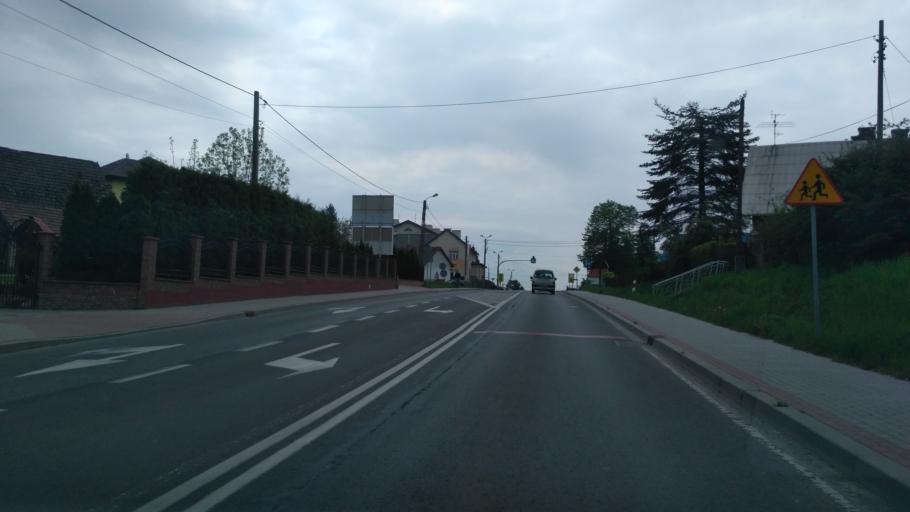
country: PL
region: Lesser Poland Voivodeship
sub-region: Powiat tarnowski
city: Tarnowiec
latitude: 49.9835
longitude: 20.9853
